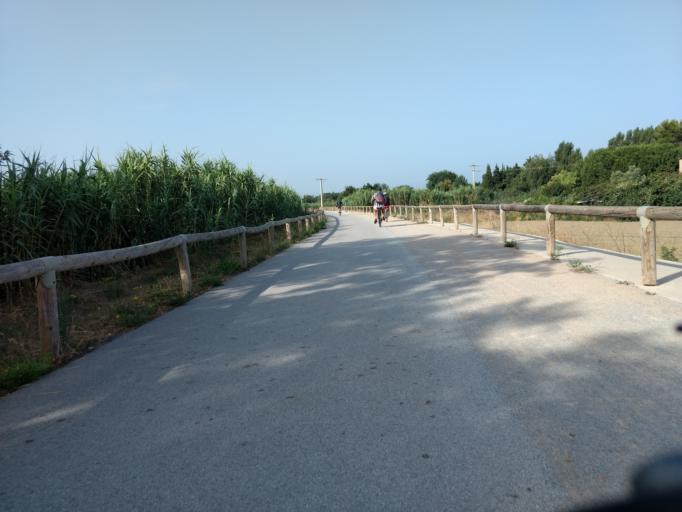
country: FR
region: Languedoc-Roussillon
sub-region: Departement des Pyrenees-Orientales
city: Claira
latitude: 42.7547
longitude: 2.9632
